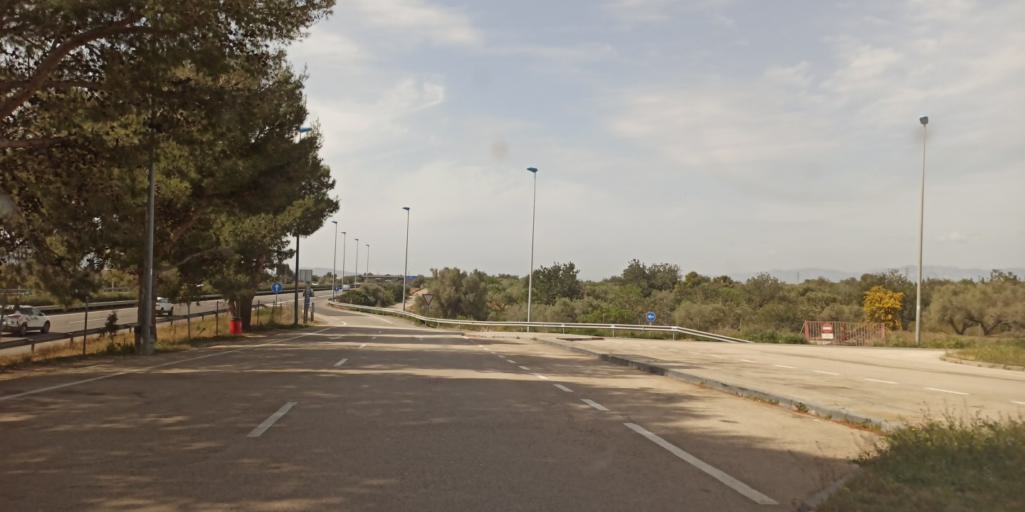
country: ES
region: Catalonia
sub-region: Provincia de Tarragona
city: Camarles
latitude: 40.7646
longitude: 0.6264
